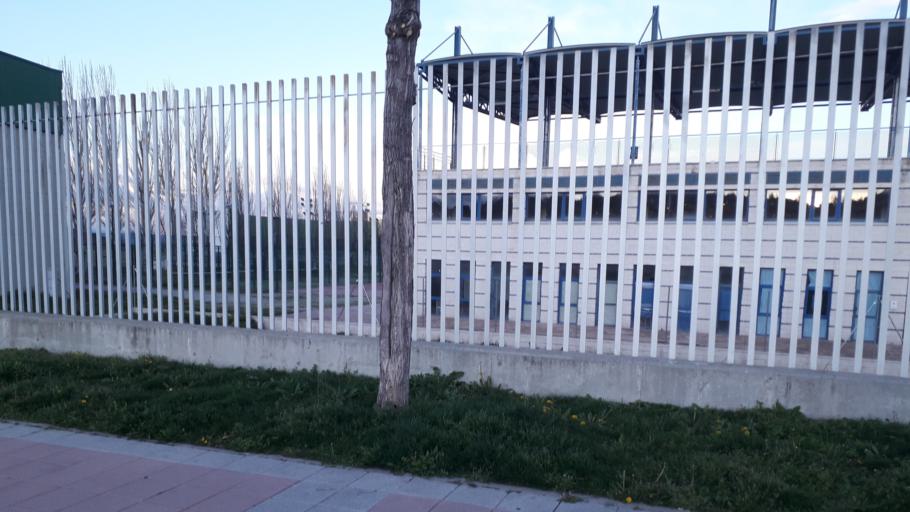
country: ES
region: Madrid
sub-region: Provincia de Madrid
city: El Molar
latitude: 40.7390
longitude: -3.5810
